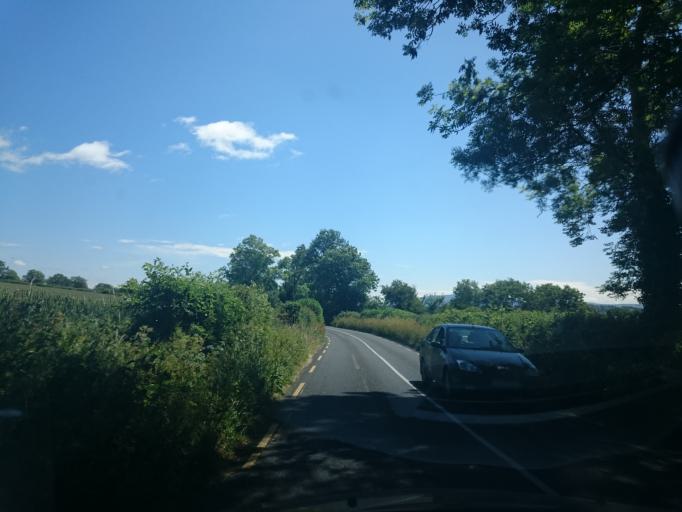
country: IE
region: Leinster
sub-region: County Carlow
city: Bagenalstown
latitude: 52.6284
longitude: -7.0311
